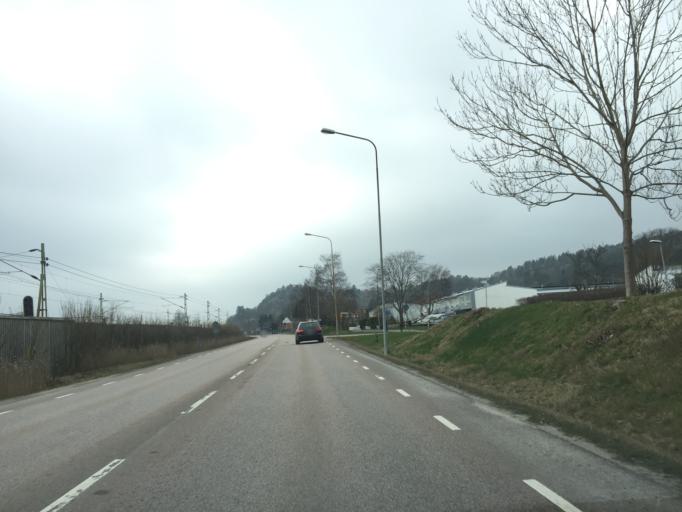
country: SE
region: Vaestra Goetaland
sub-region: Partille Kommun
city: Partille
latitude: 57.7442
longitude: 12.1177
